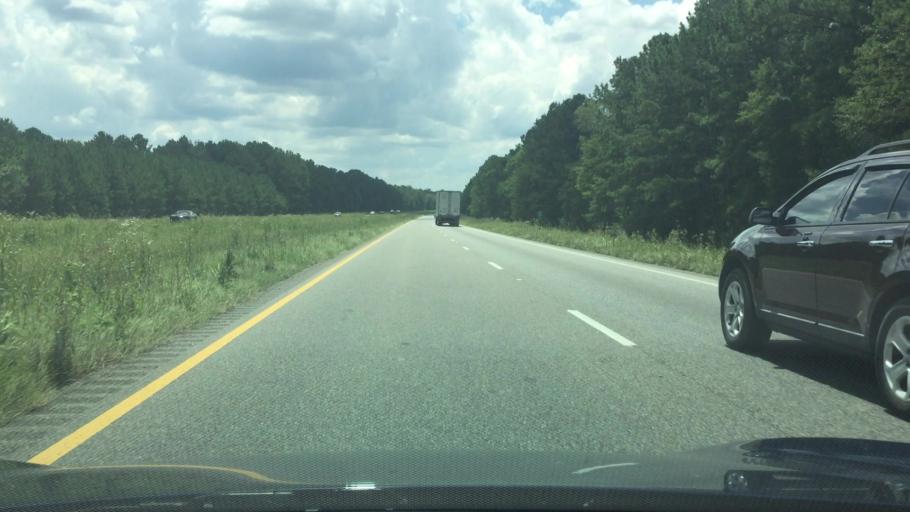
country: US
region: Alabama
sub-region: Pike County
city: Troy
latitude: 32.0017
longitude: -86.0281
